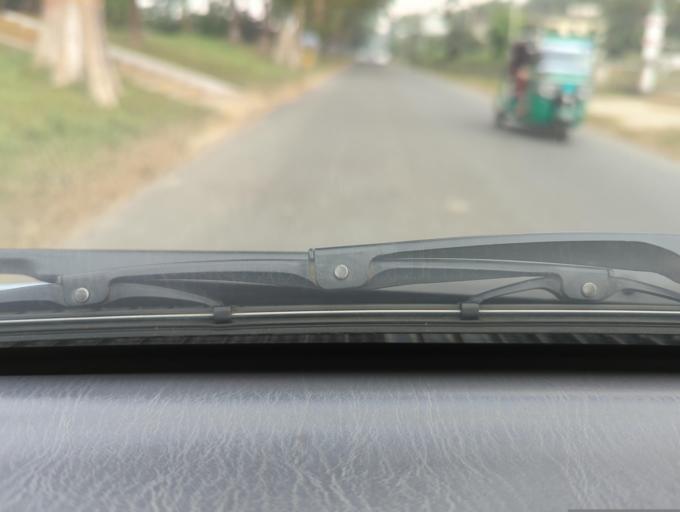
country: BD
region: Sylhet
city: Maulavi Bazar
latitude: 24.5093
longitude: 91.7285
